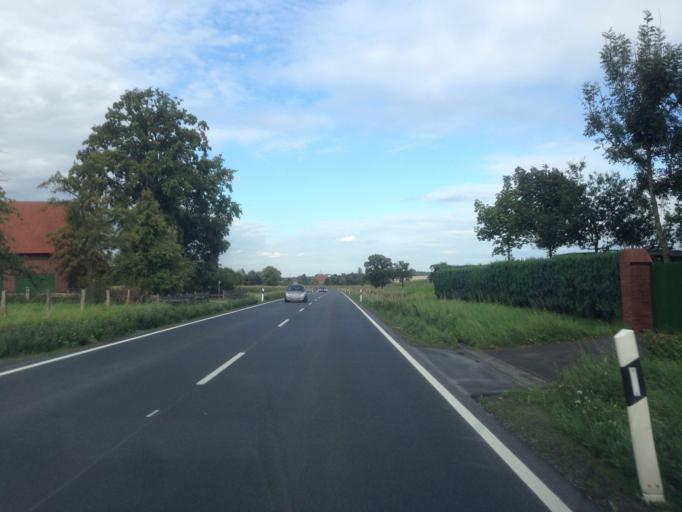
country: DE
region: North Rhine-Westphalia
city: Ludinghausen
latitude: 51.7428
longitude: 7.4204
